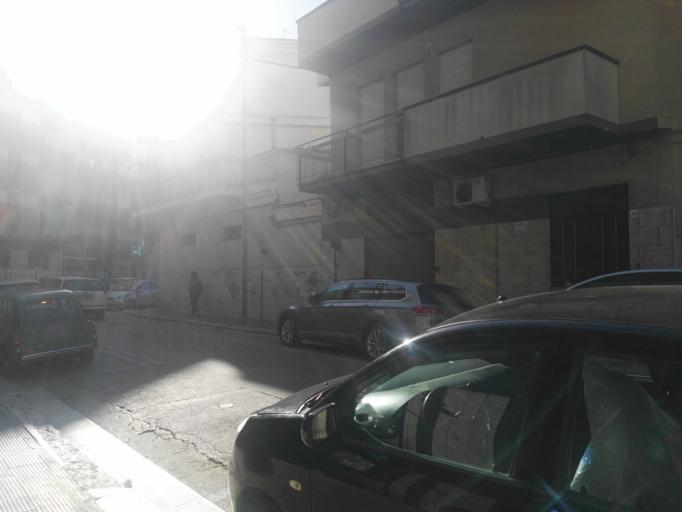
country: IT
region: Apulia
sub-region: Provincia di Barletta - Andria - Trani
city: Andria
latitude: 41.2292
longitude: 16.3056
